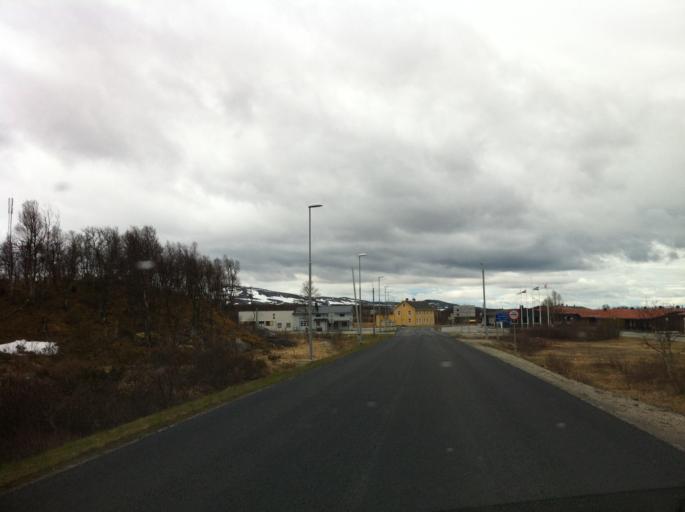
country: NO
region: Sor-Trondelag
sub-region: Tydal
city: Aas
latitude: 62.6412
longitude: 12.0354
